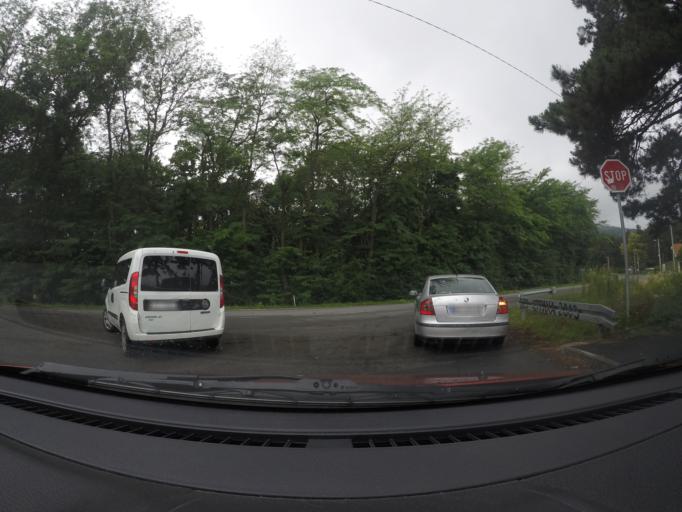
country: RS
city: Rusanj
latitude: 44.6809
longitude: 20.5330
